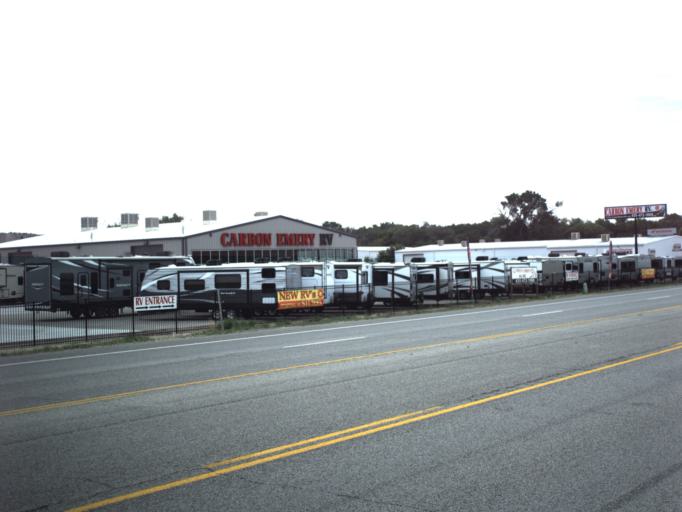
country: US
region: Utah
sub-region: Carbon County
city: Spring Glen
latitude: 39.6683
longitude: -110.8614
